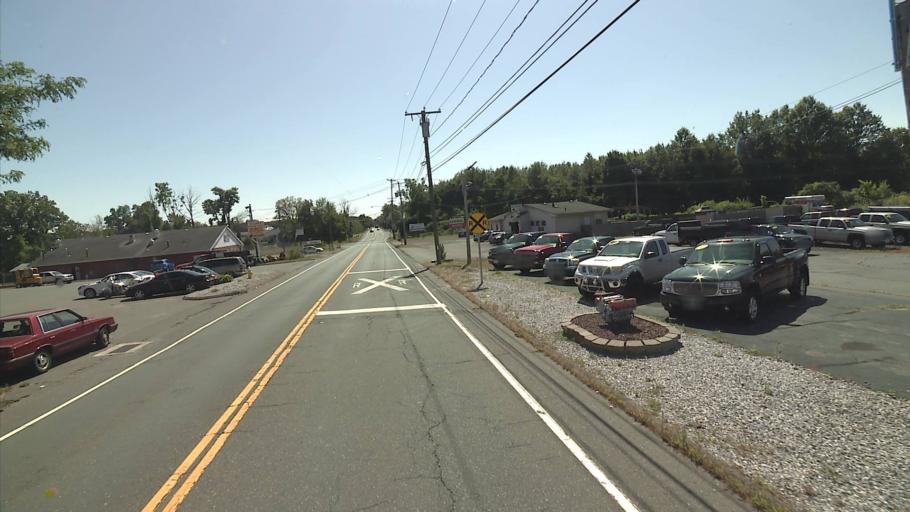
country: US
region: Connecticut
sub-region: Hartford County
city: Windsor Locks
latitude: 41.9499
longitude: -72.6280
